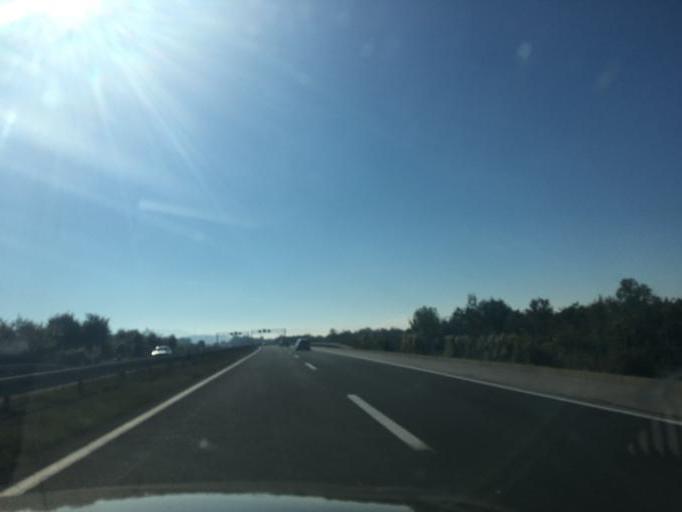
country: HR
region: Licko-Senjska
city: Gospic
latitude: 44.6800
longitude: 15.4097
